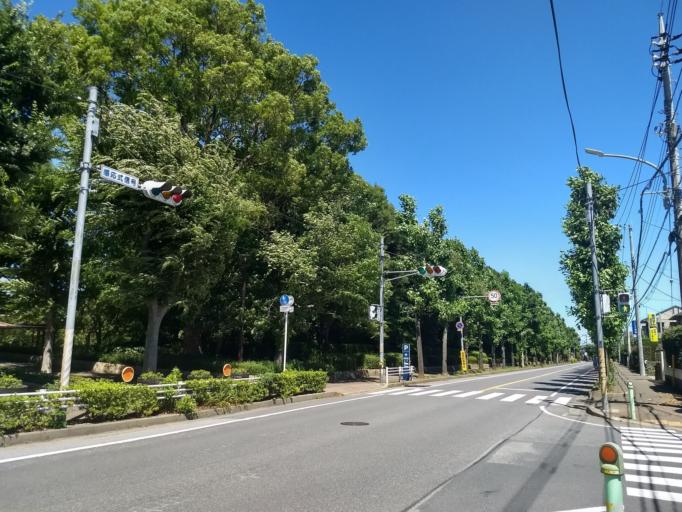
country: JP
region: Chiba
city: Kashiwa
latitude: 35.8926
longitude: 139.9381
